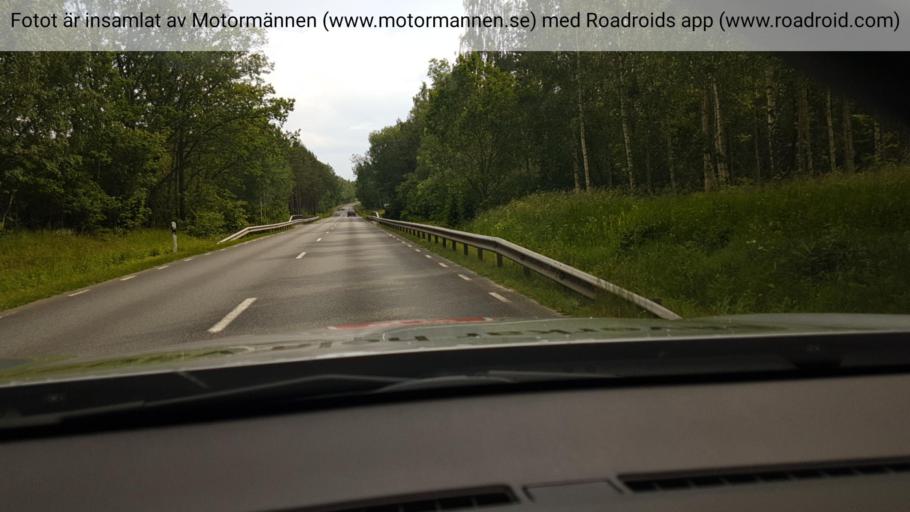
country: SE
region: Vaestra Goetaland
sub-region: Hjo Kommun
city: Hjo
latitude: 58.1059
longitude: 14.2082
